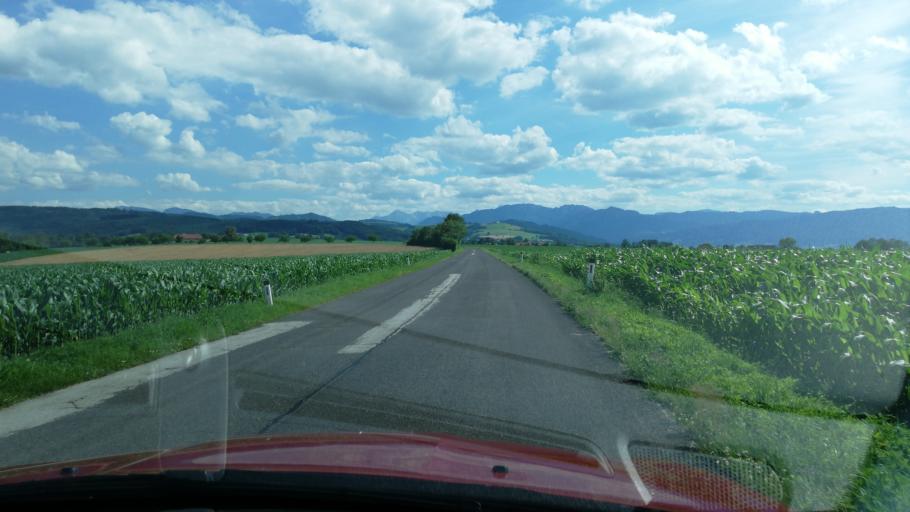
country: AT
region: Upper Austria
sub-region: Politischer Bezirk Steyr-Land
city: Pfarrkirchen bei Bad Hall
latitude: 47.9954
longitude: 14.1627
